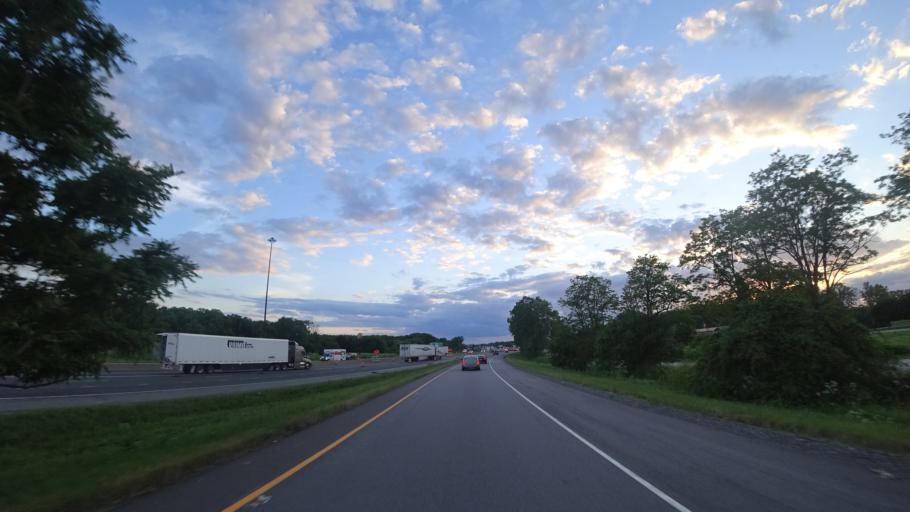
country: US
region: Indiana
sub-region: Porter County
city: Ogden Dunes
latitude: 41.6024
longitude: -87.1761
